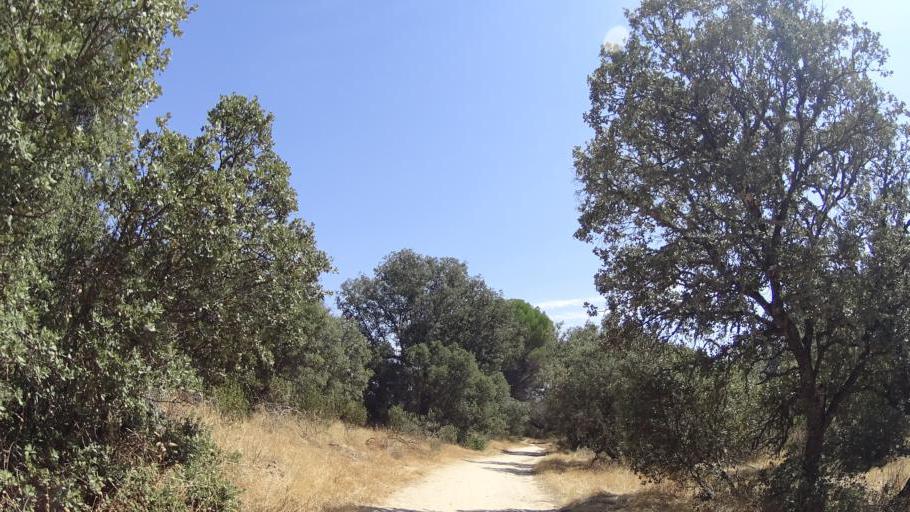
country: ES
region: Madrid
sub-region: Provincia de Madrid
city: Boadilla del Monte
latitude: 40.4245
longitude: -3.8568
